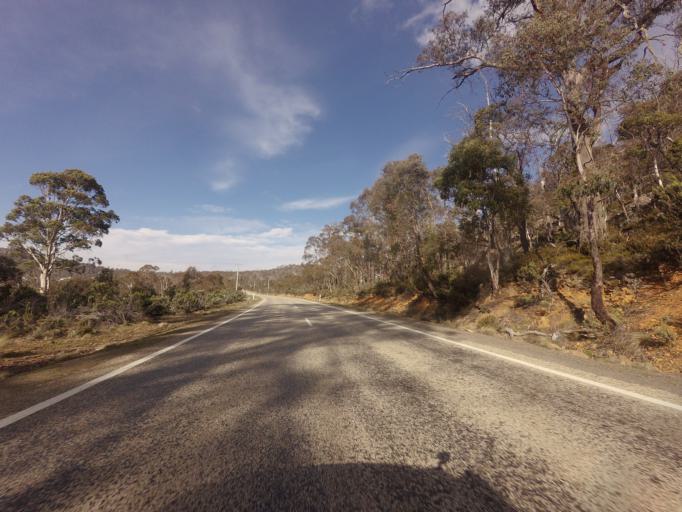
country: AU
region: Tasmania
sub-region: Meander Valley
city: Deloraine
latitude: -41.9900
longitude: 146.6827
